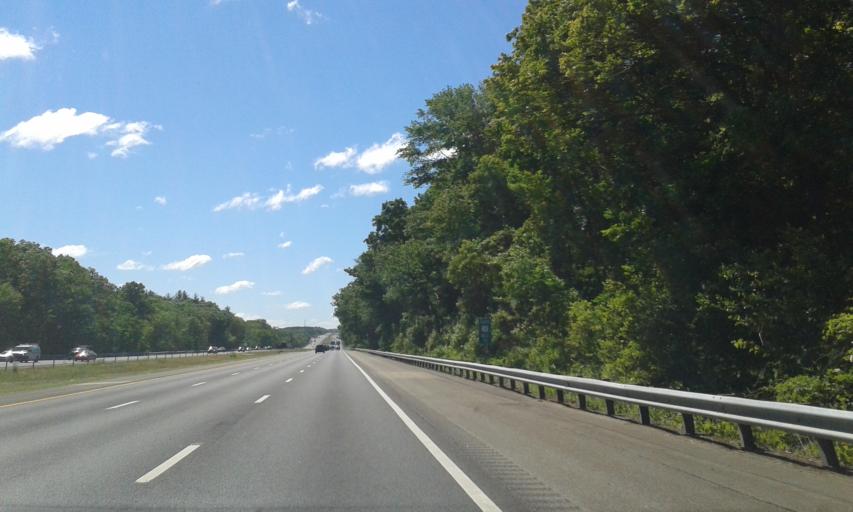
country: US
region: Massachusetts
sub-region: Middlesex County
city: Bedford
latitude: 42.5171
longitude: -71.2588
